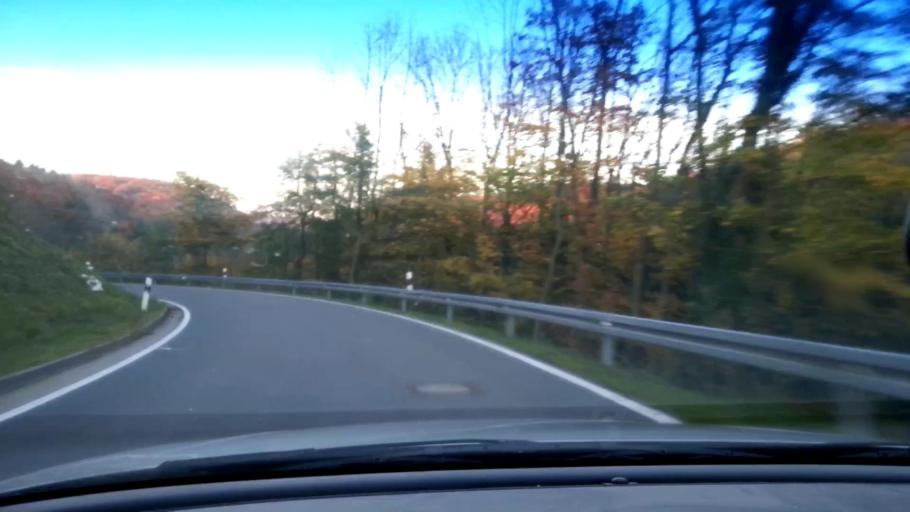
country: DE
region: Bavaria
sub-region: Upper Franconia
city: Heiligenstadt
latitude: 49.8593
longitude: 11.1213
